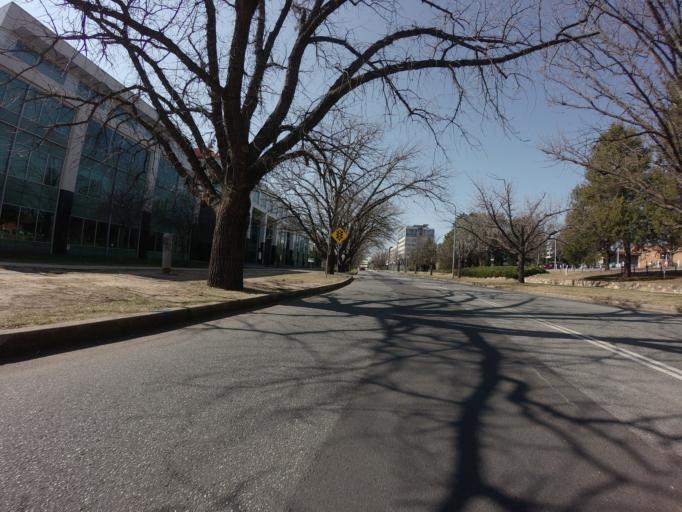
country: AU
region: Australian Capital Territory
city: Forrest
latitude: -35.3136
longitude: 149.1309
